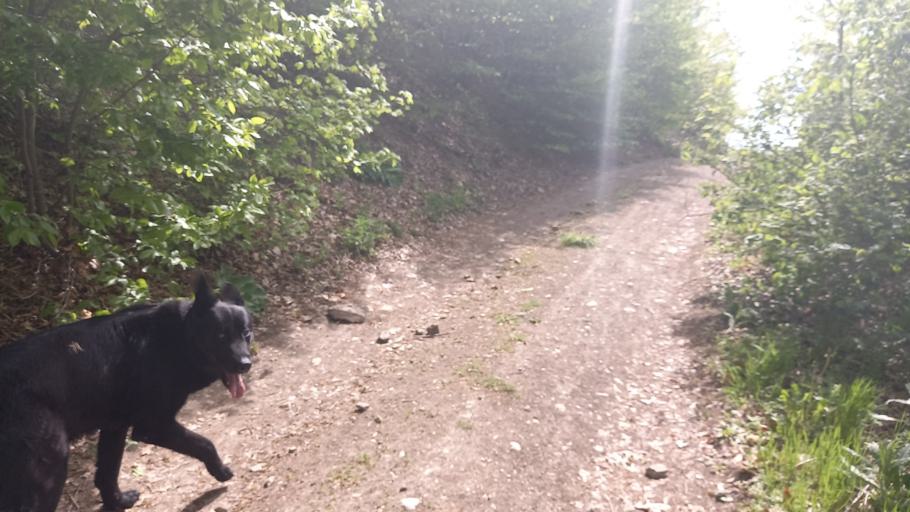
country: RU
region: Stavropol'skiy
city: Zheleznovodsk
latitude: 44.0908
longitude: 43.0298
